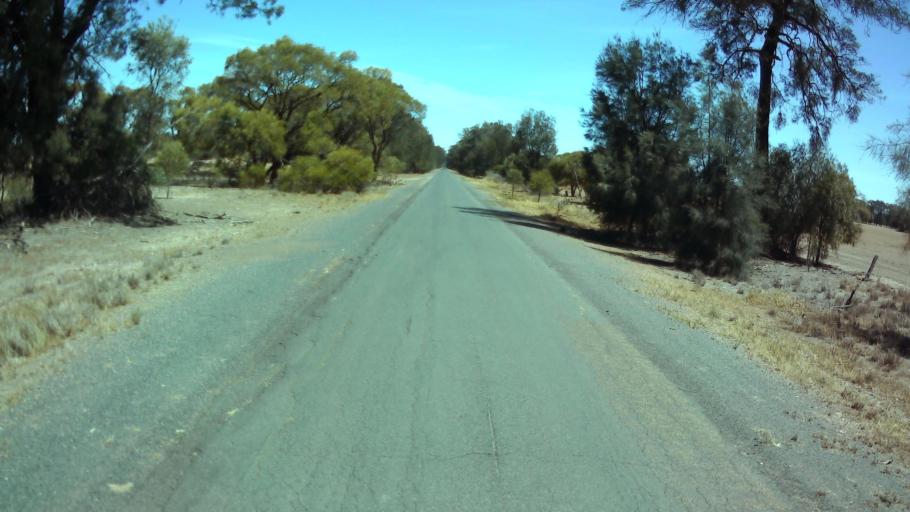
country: AU
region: New South Wales
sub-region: Weddin
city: Grenfell
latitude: -33.8750
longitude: 147.6912
